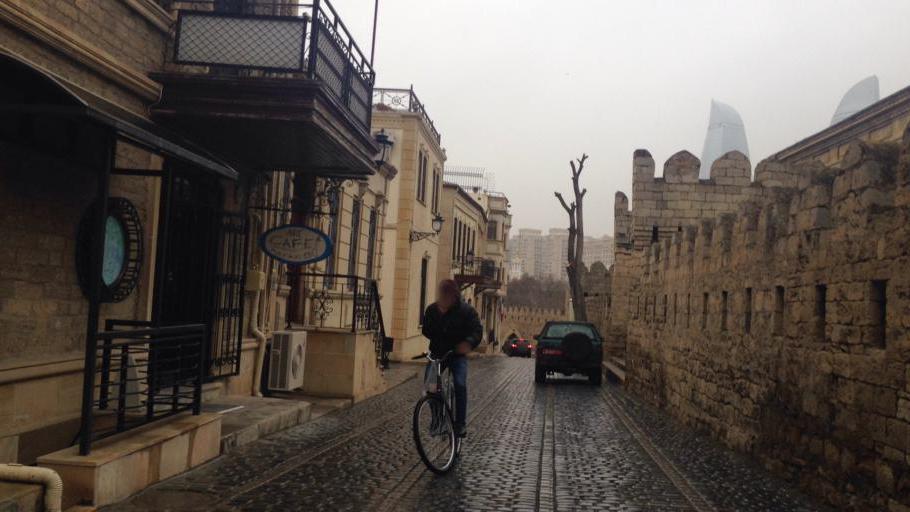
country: AZ
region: Baki
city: Badamdar
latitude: 40.3669
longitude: 49.8323
